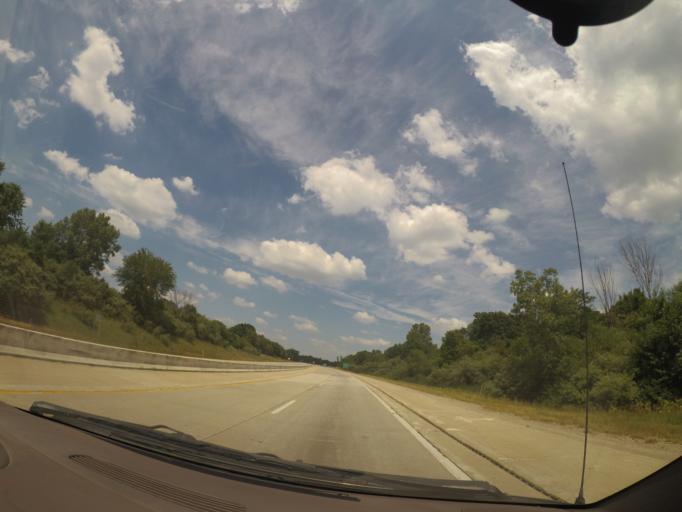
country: US
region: Indiana
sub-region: Elkhart County
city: Dunlap
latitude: 41.6597
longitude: -85.9034
